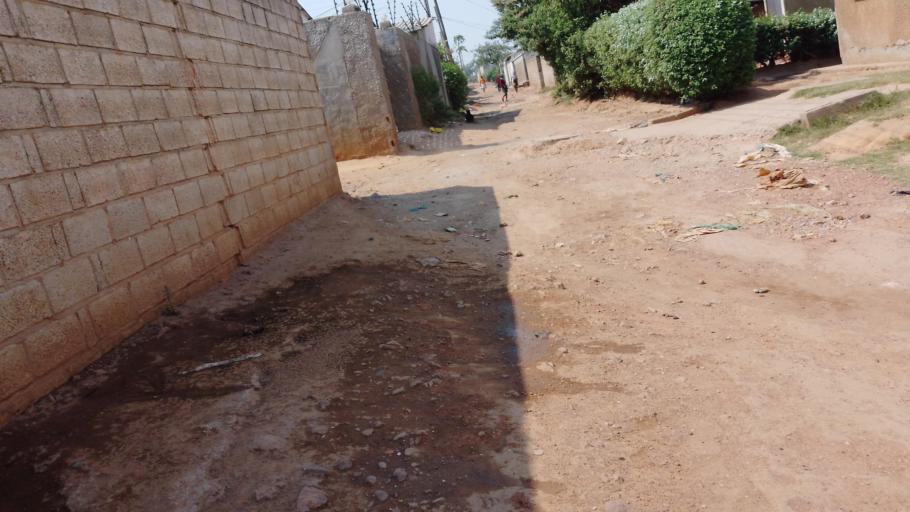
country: ZM
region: Lusaka
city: Lusaka
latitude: -15.3969
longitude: 28.3694
